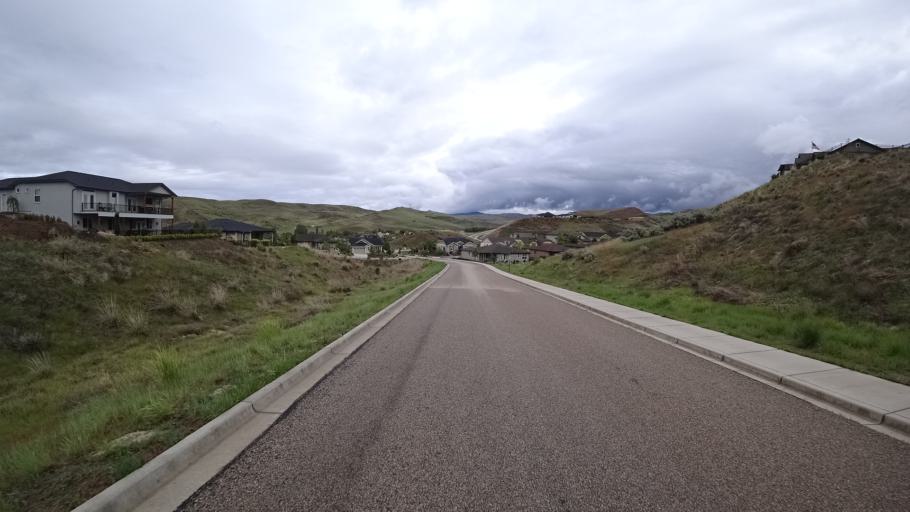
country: US
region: Idaho
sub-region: Ada County
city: Eagle
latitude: 43.7715
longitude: -116.2590
